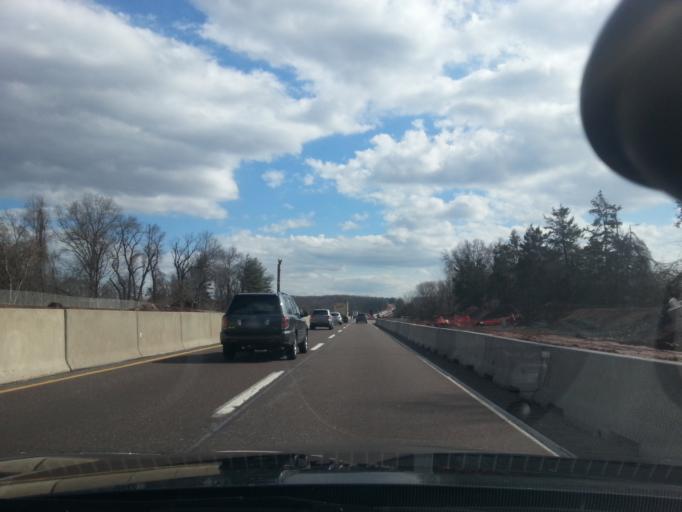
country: US
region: Pennsylvania
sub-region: Montgomery County
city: Kulpsville
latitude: 40.2074
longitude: -75.3222
